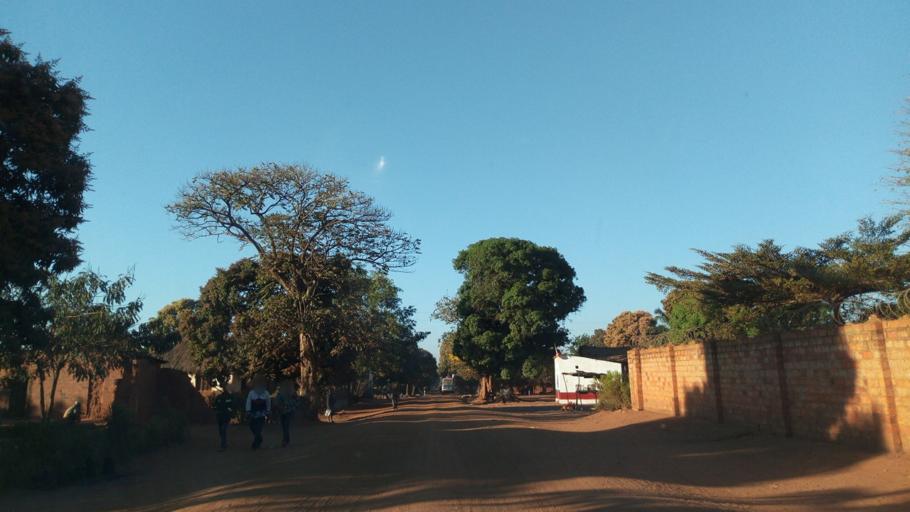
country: ZM
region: Luapula
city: Mwense
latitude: -10.3754
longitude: 28.6140
